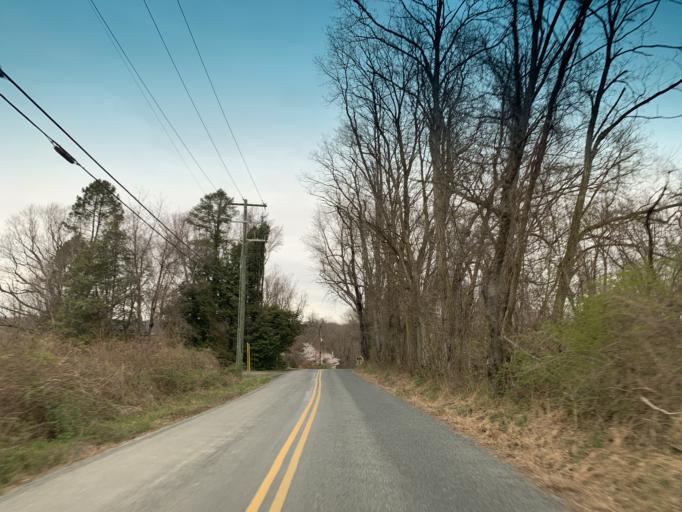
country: US
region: Maryland
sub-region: Harford County
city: Aberdeen
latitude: 39.5368
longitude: -76.2018
